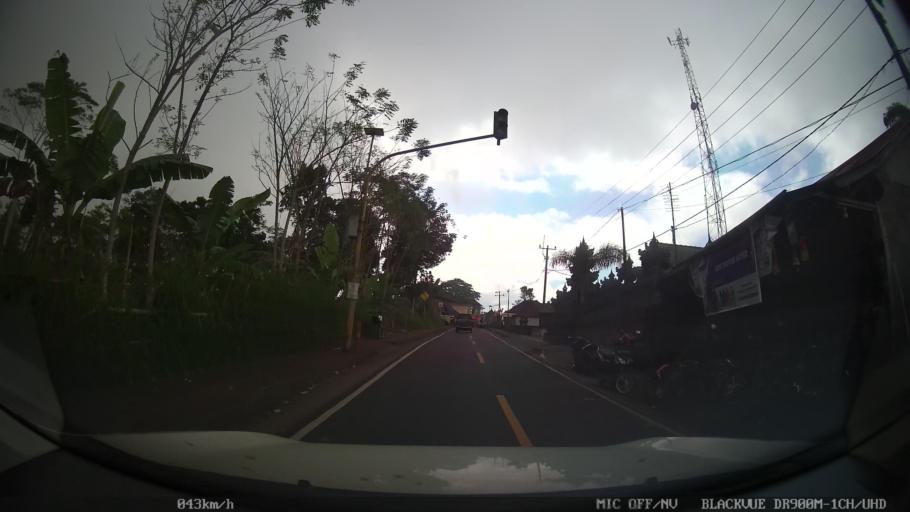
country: ID
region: Bali
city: Banjar Suter
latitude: -8.3093
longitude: 115.3966
